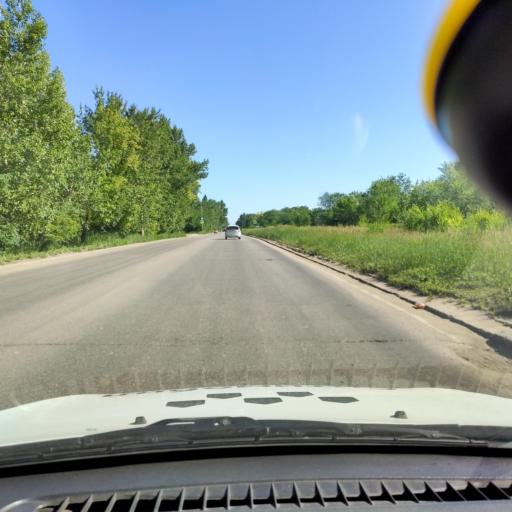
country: RU
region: Samara
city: Podstepki
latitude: 53.5742
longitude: 49.2189
